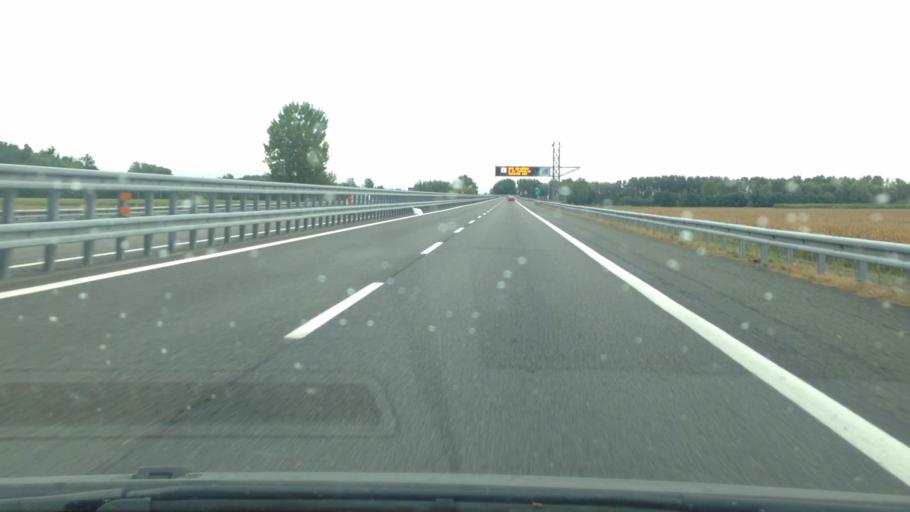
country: IT
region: Piedmont
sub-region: Provincia di Alessandria
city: Pietra Marazzi
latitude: 44.9361
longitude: 8.6553
